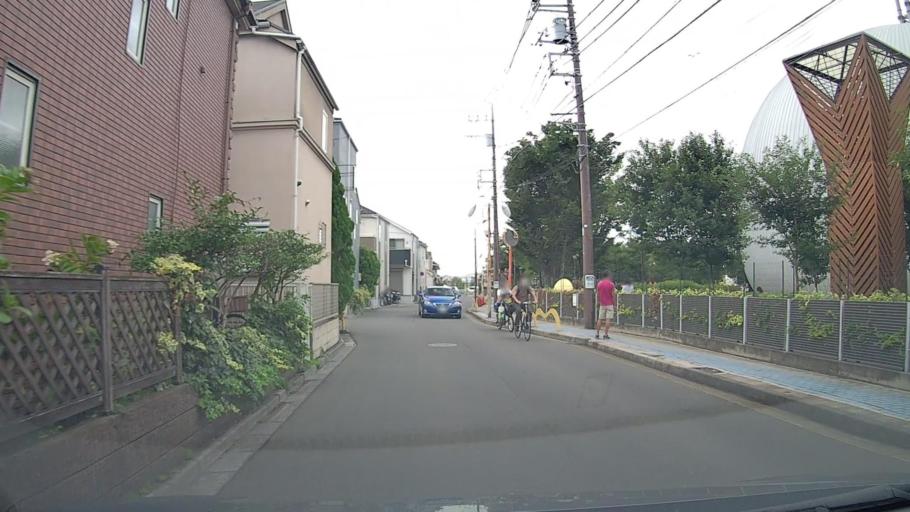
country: JP
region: Tokyo
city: Tanashicho
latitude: 35.7340
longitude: 139.5234
